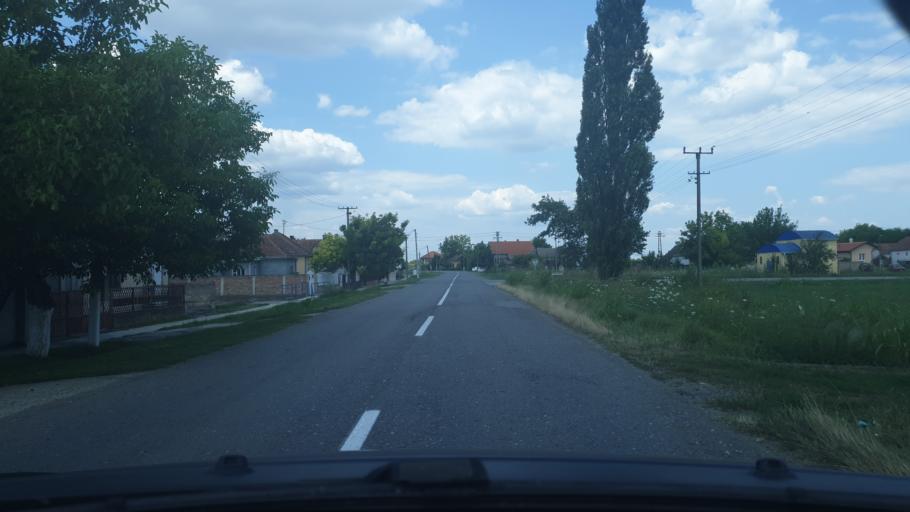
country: RS
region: Autonomna Pokrajina Vojvodina
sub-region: Sremski Okrug
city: Pecinci
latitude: 44.8471
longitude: 19.9615
